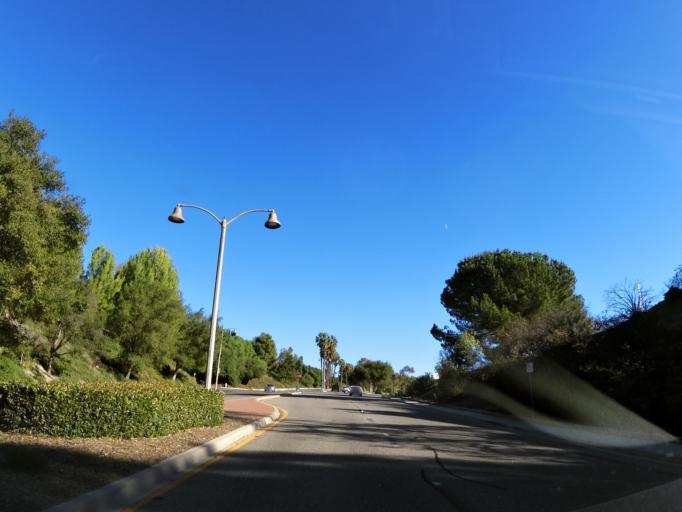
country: US
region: California
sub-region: Ventura County
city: Thousand Oaks
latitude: 34.2263
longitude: -118.8439
